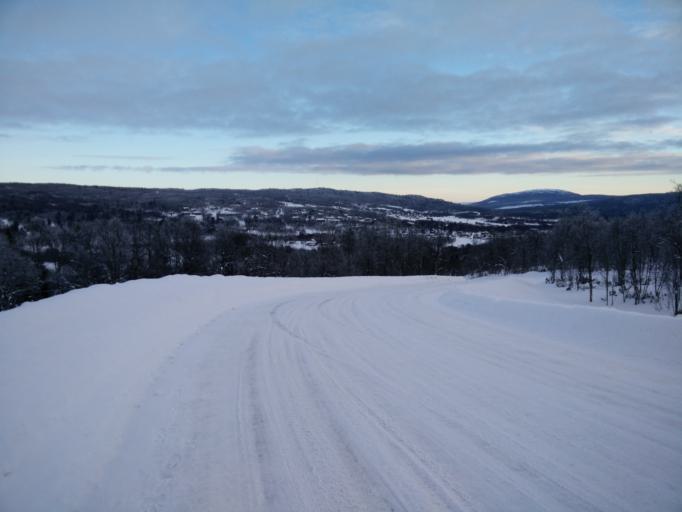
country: NO
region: Sor-Trondelag
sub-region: Tydal
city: Aas
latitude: 62.6521
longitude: 12.4088
